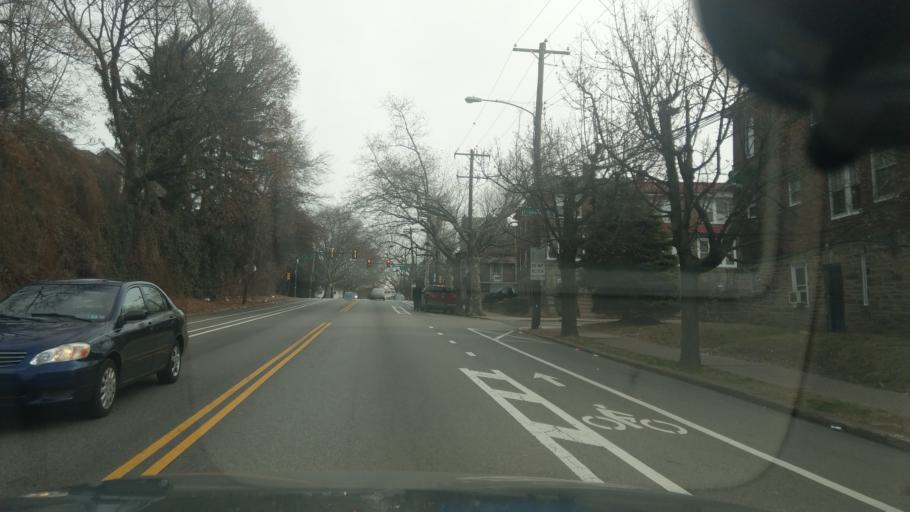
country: US
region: Pennsylvania
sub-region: Montgomery County
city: Jenkintown
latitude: 40.0461
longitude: -75.1337
